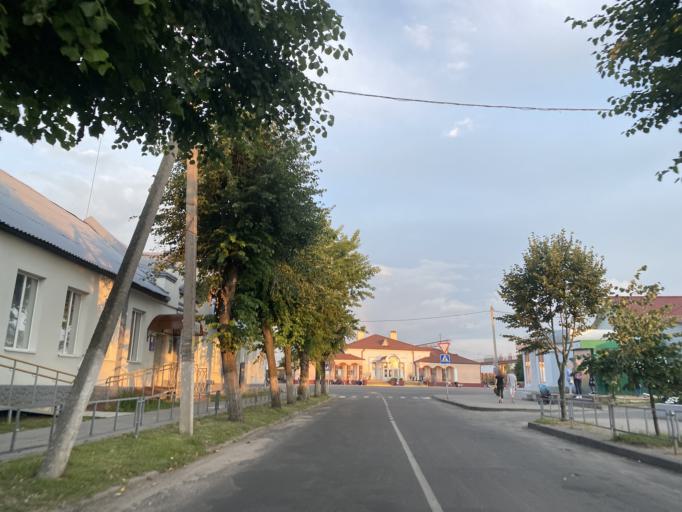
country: BY
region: Brest
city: Ivatsevichy
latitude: 52.7103
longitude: 25.3441
